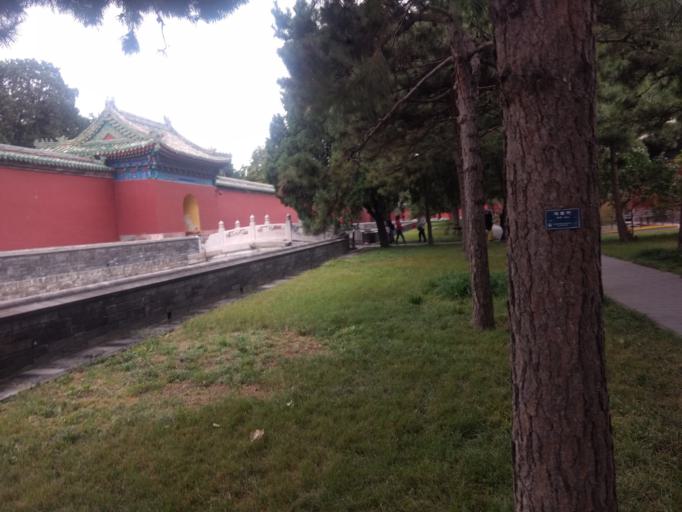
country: CN
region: Beijing
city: Longtan
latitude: 39.8790
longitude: 116.4011
